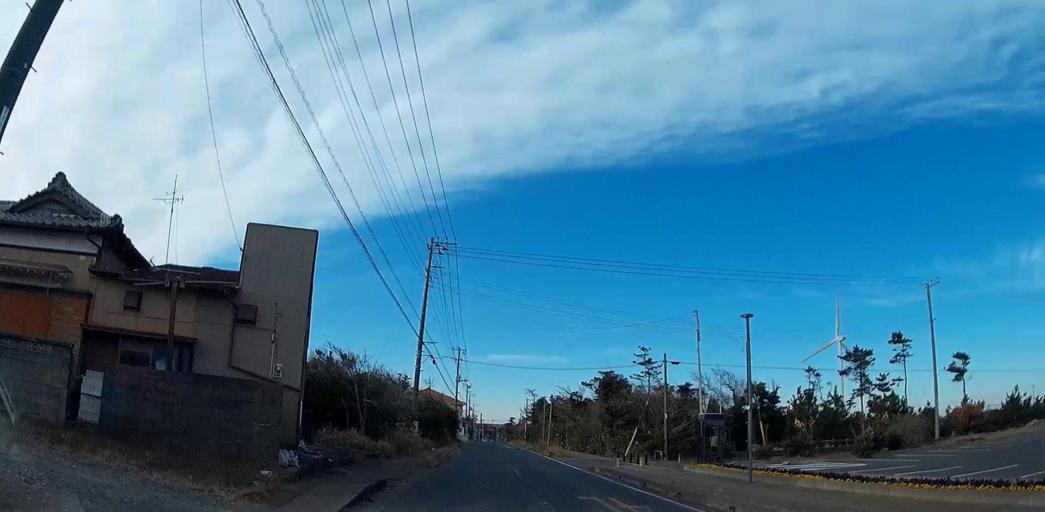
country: JP
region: Chiba
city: Hasaki
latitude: 35.7492
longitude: 140.8320
